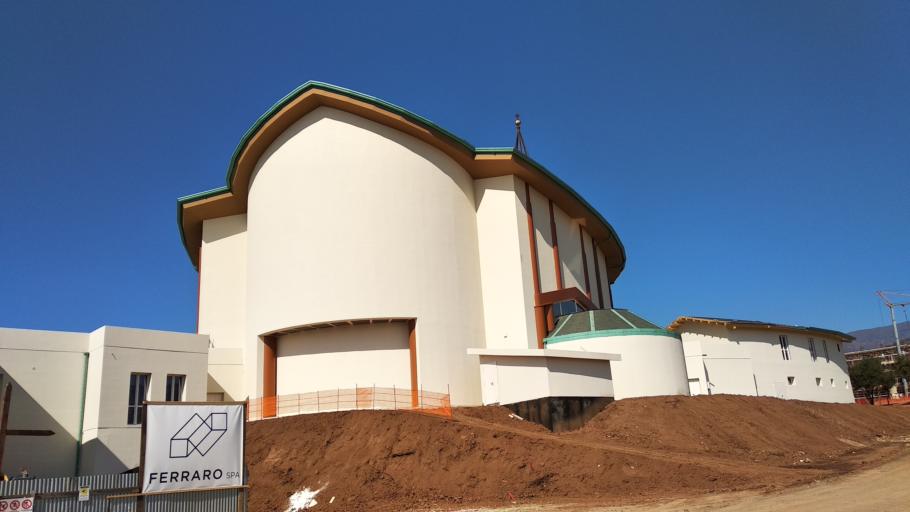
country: IT
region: Calabria
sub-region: Provincia di Catanzaro
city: Nicastro-Sambiase
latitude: 38.9585
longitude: 16.2958
